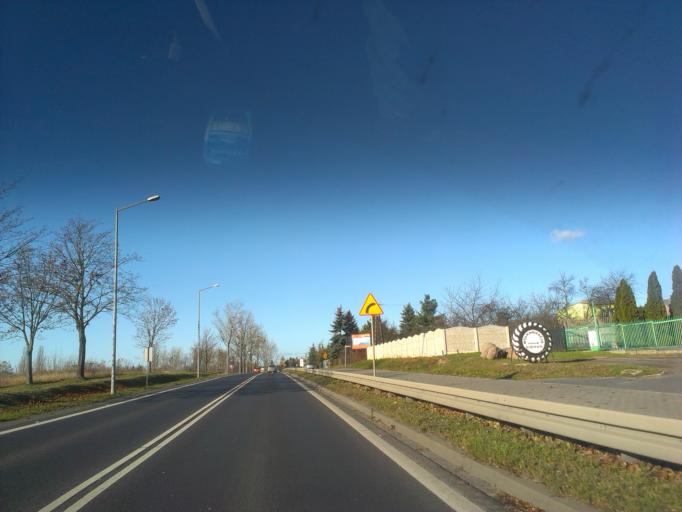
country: PL
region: Greater Poland Voivodeship
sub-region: Powiat poznanski
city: Zlotniki
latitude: 52.4891
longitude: 16.8500
